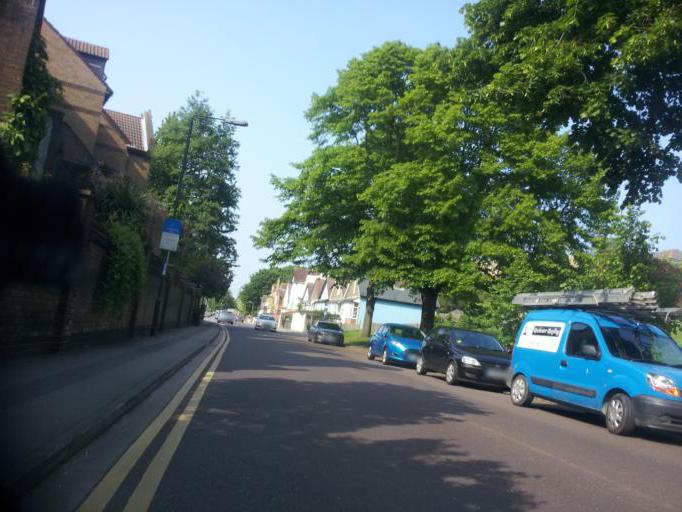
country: GB
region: England
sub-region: Medway
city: Rochester
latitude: 51.3862
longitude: 0.4981
